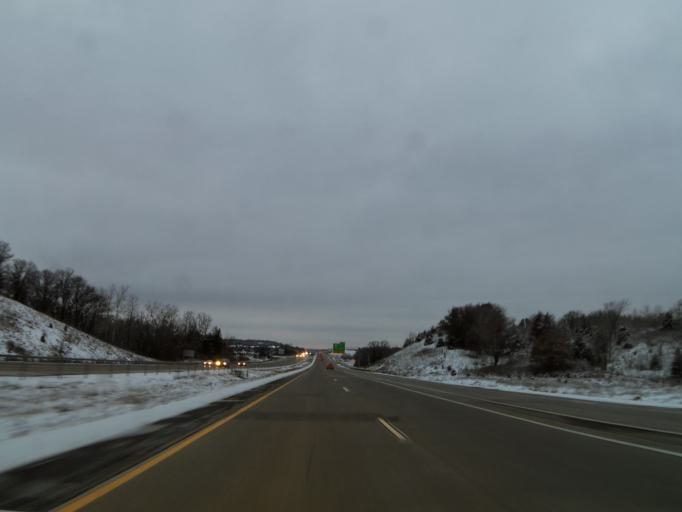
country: US
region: Wisconsin
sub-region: Saint Croix County
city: Hudson
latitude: 44.9640
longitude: -92.6851
